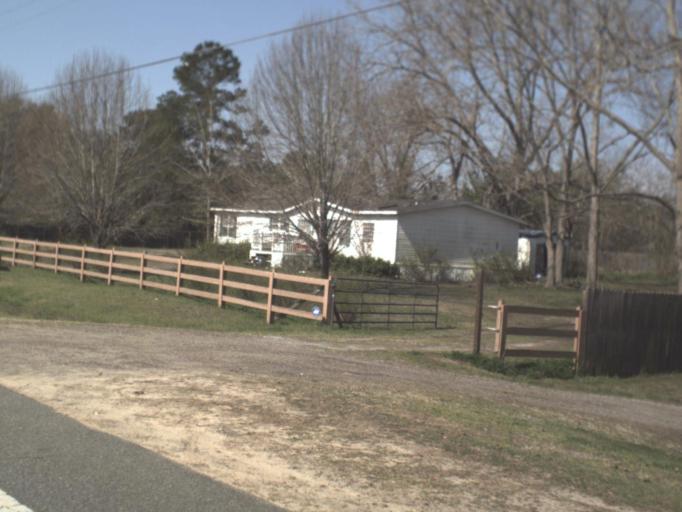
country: US
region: Florida
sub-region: Gadsden County
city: Havana
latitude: 30.6181
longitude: -84.4385
